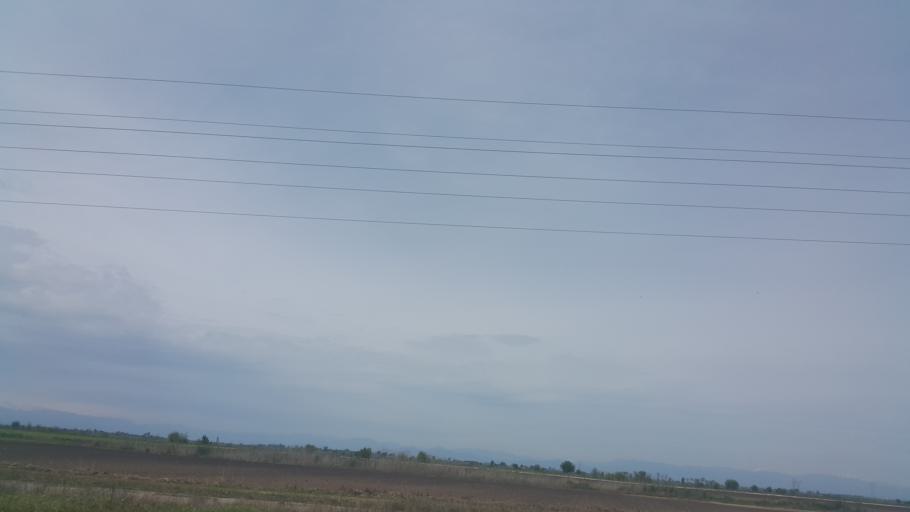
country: TR
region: Adana
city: Kosreli
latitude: 37.0634
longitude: 35.9467
